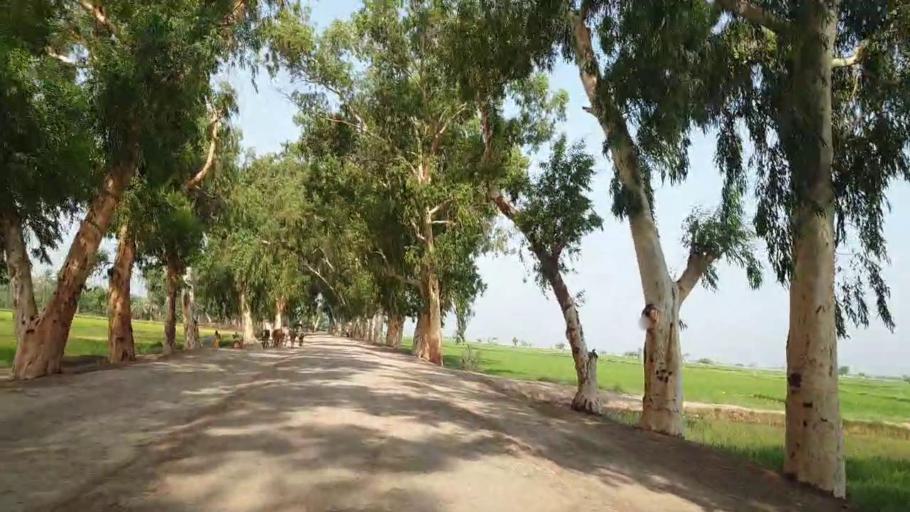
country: PK
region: Sindh
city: Lakhi
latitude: 27.8159
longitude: 68.7340
